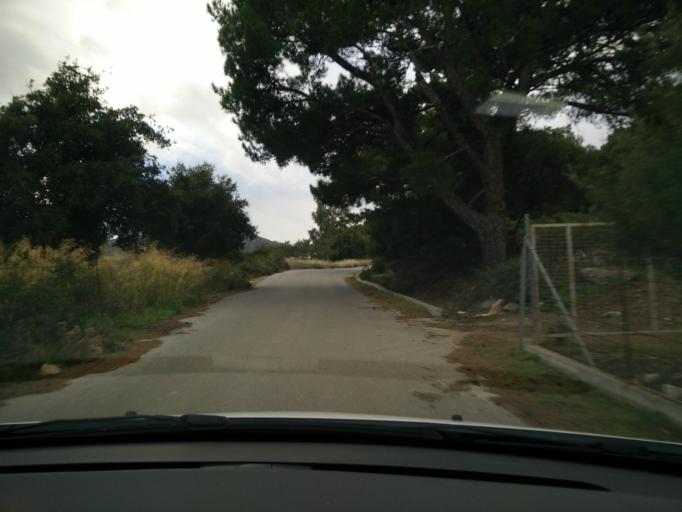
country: GR
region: Crete
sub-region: Nomos Lasithiou
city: Kritsa
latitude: 35.1032
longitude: 25.6940
